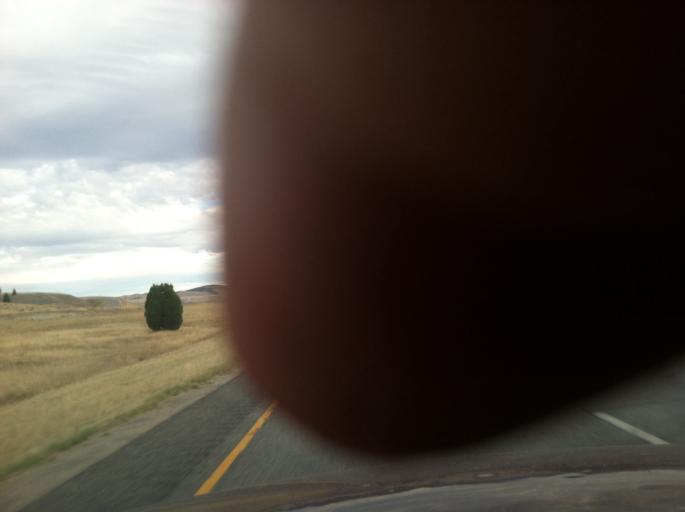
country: US
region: Montana
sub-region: Silver Bow County
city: Butte-Silver Bow (Balance)
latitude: 46.0128
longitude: -112.7132
